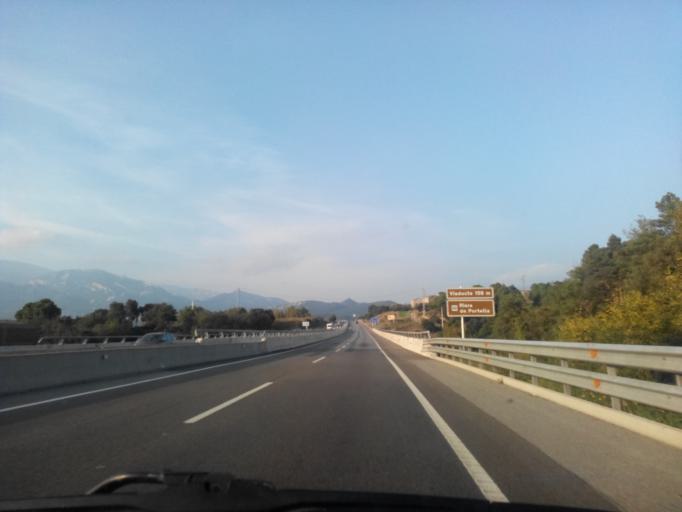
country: ES
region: Catalonia
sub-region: Provincia de Barcelona
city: Gironella
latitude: 42.0583
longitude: 1.8757
